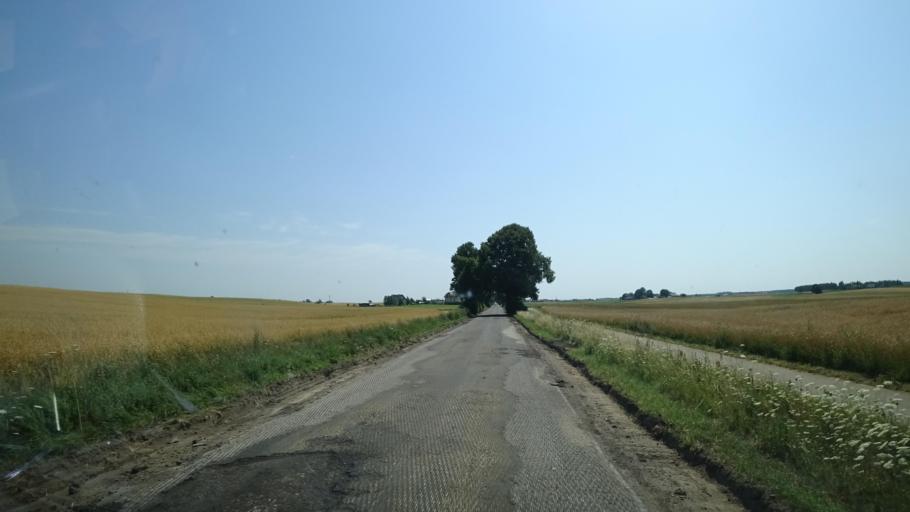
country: PL
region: Pomeranian Voivodeship
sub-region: Powiat chojnicki
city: Brusy
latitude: 53.8759
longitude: 17.6566
